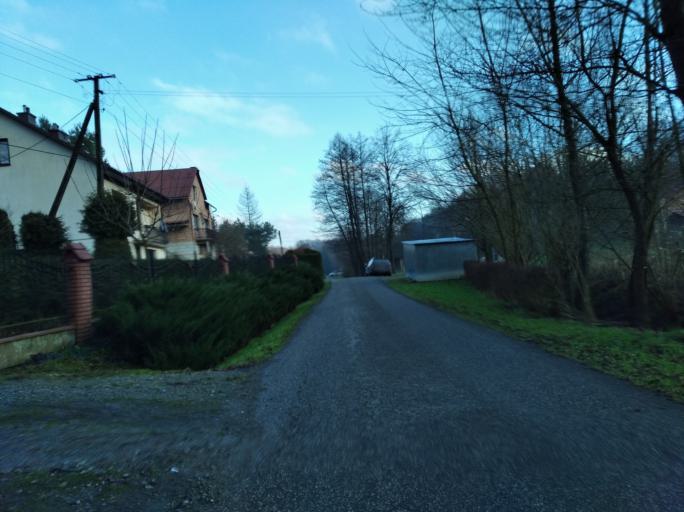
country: PL
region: Subcarpathian Voivodeship
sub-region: Powiat strzyzowski
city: Czudec
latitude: 49.9499
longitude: 21.7965
